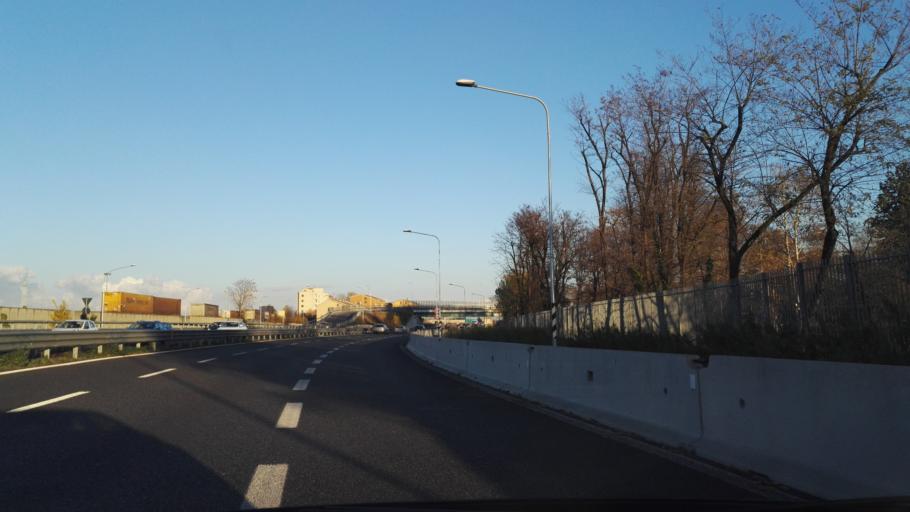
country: IT
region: Lombardy
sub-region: Citta metropolitana di Milano
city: Novegro-Tregarezzo-San Felice
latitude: 45.4763
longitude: 9.2925
